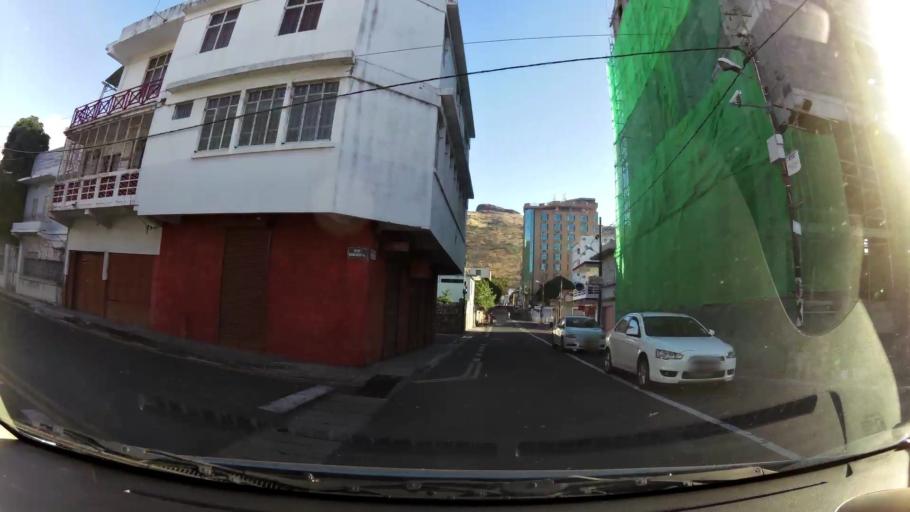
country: MU
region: Port Louis
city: Port Louis
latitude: -20.1683
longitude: 57.5058
